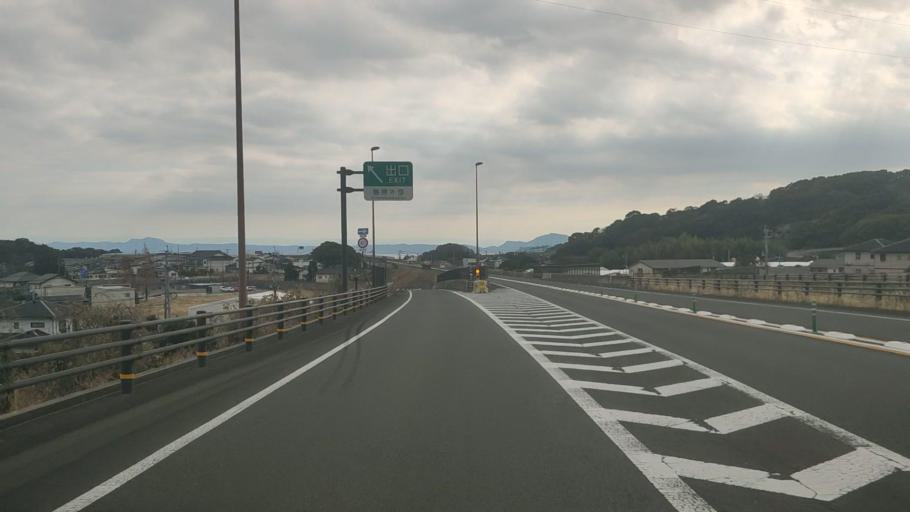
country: JP
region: Nagasaki
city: Shimabara
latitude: 32.7633
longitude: 130.3621
